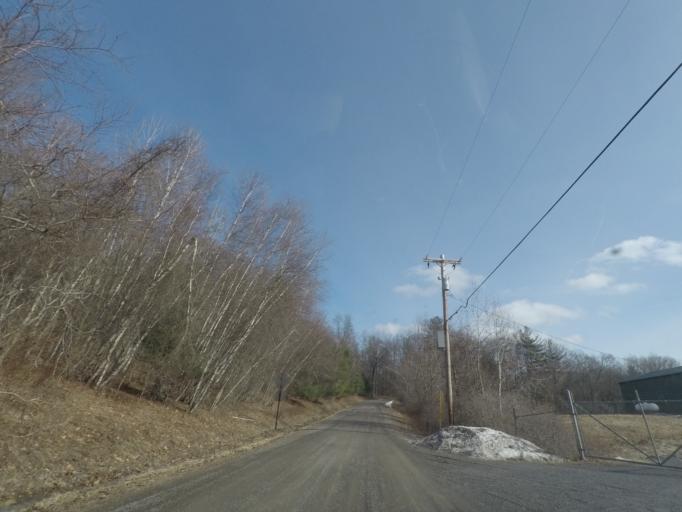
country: US
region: New York
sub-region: Rensselaer County
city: Nassau
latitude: 42.5610
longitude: -73.5606
